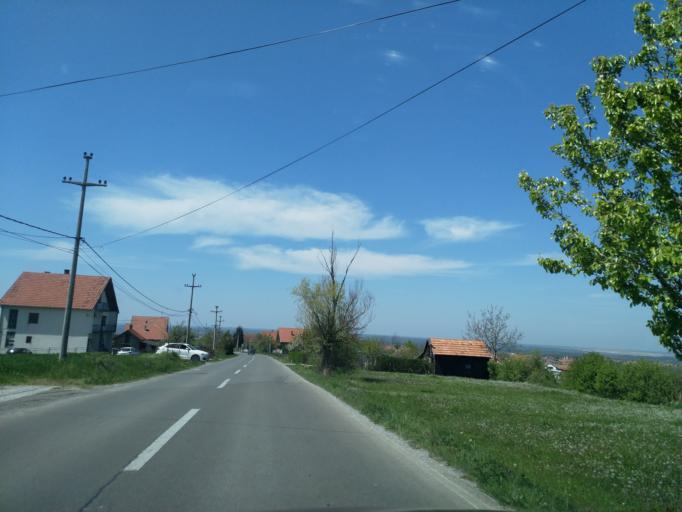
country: RS
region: Central Serbia
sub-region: Belgrade
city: Lazarevac
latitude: 44.3741
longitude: 20.2967
